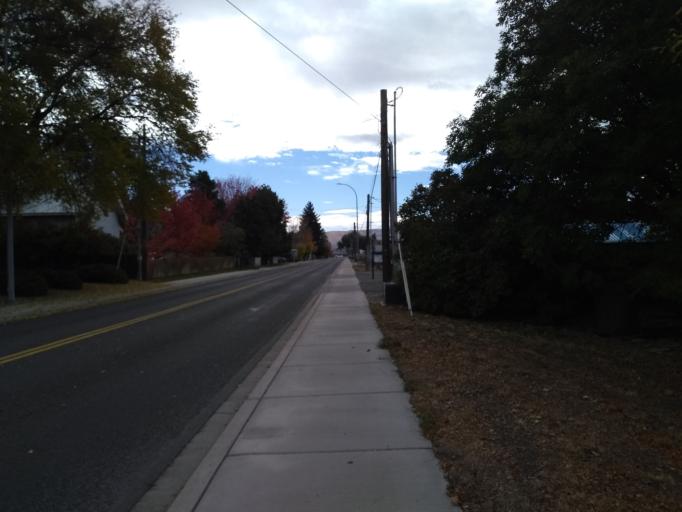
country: US
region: Washington
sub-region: Kittitas County
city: Ellensburg
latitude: 46.9878
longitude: -120.5446
